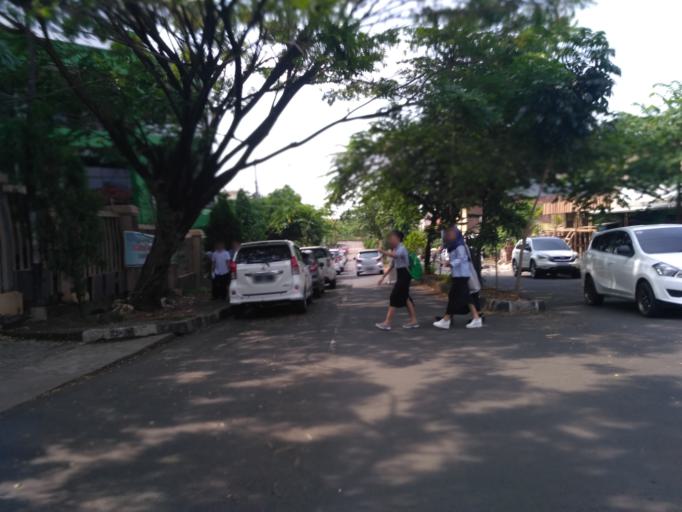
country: ID
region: Central Java
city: Semarang
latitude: -7.0504
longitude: 110.4445
